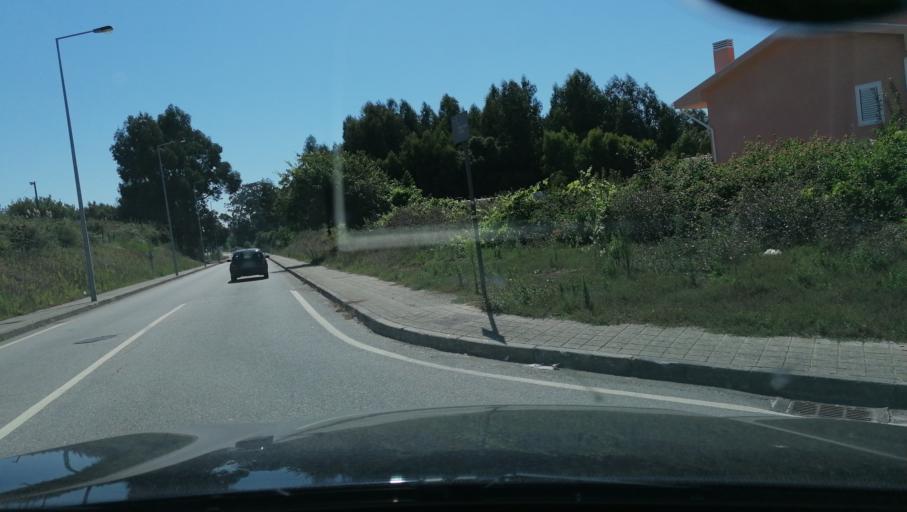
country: PT
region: Porto
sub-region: Vila Nova de Gaia
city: Vila Nova da Telha
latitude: 41.0782
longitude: -8.6402
